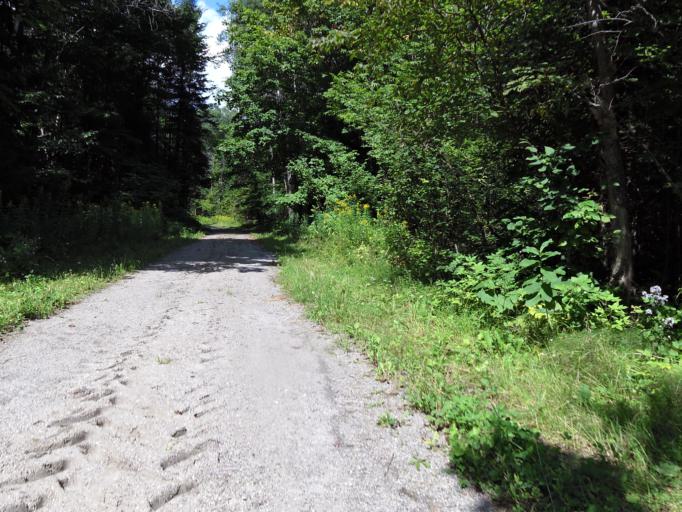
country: CA
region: Quebec
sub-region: Outaouais
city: Wakefield
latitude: 45.8163
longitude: -75.9628
